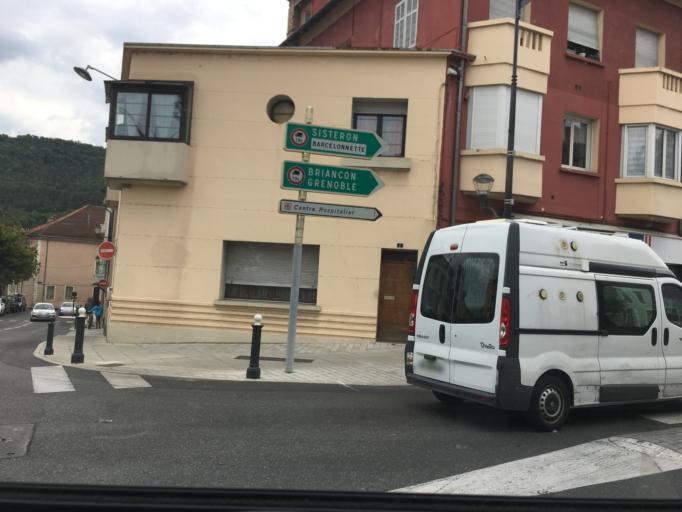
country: FR
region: Provence-Alpes-Cote d'Azur
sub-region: Departement des Hautes-Alpes
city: Gap
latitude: 44.5598
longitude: 6.0759
